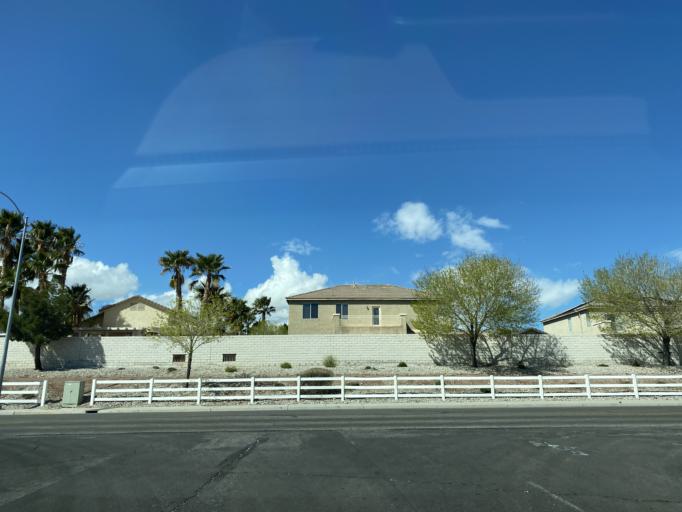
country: US
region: Nevada
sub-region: Clark County
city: Summerlin South
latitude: 36.3196
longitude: -115.2873
